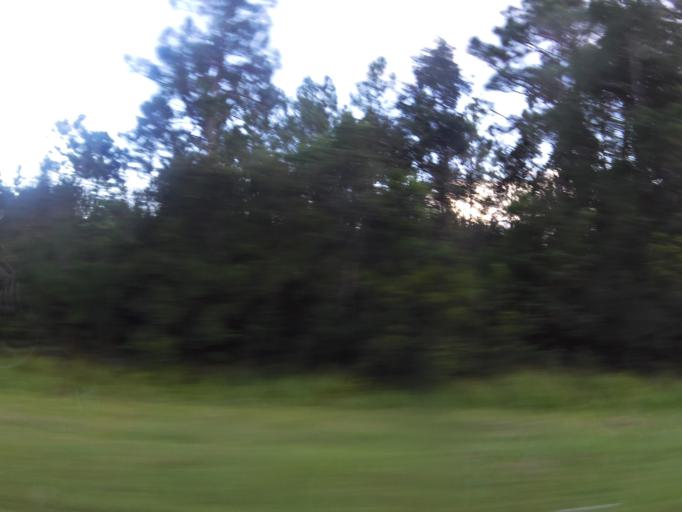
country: US
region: Georgia
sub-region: Camden County
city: St Marys
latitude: 30.7620
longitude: -81.6346
